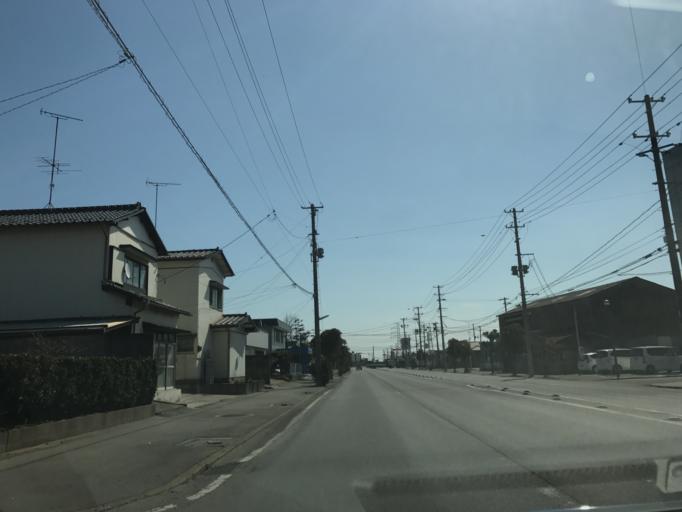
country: JP
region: Fukushima
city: Iwaki
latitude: 36.9442
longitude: 140.8735
